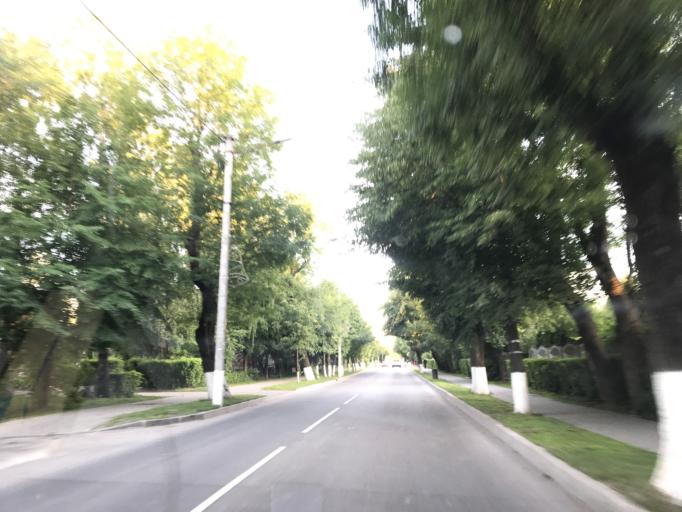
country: RU
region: Kaliningrad
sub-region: Zelenogradskiy Rayon
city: Zelenogradsk
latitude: 54.9559
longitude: 20.4711
